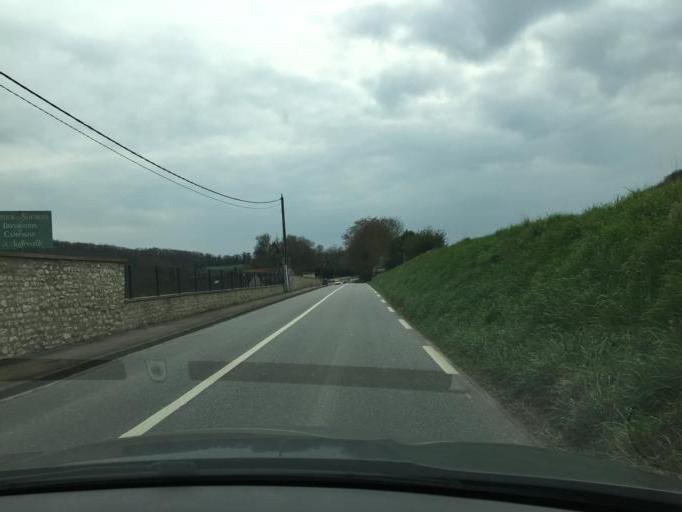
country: FR
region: Ile-de-France
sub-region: Departement des Yvelines
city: Mantes-la-Ville
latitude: 48.9580
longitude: 1.7076
